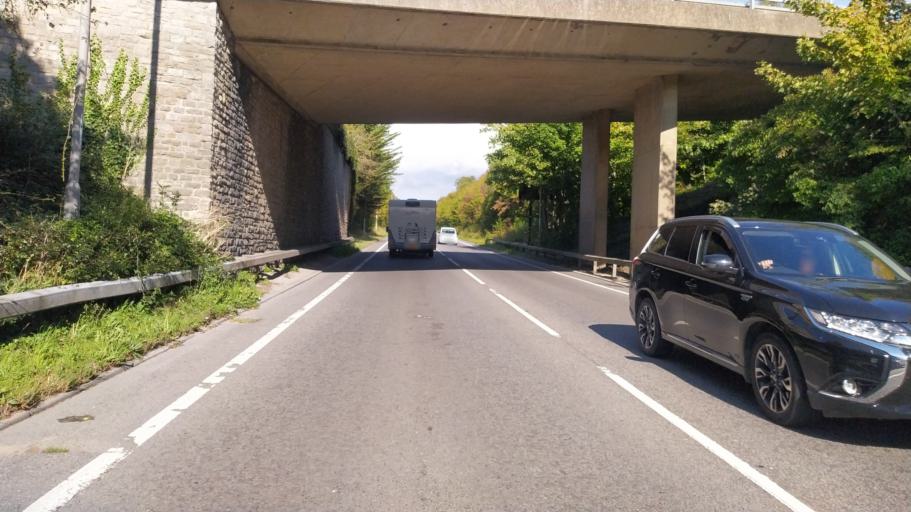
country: GB
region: England
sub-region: Dorset
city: Weymouth
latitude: 50.6299
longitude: -2.4713
